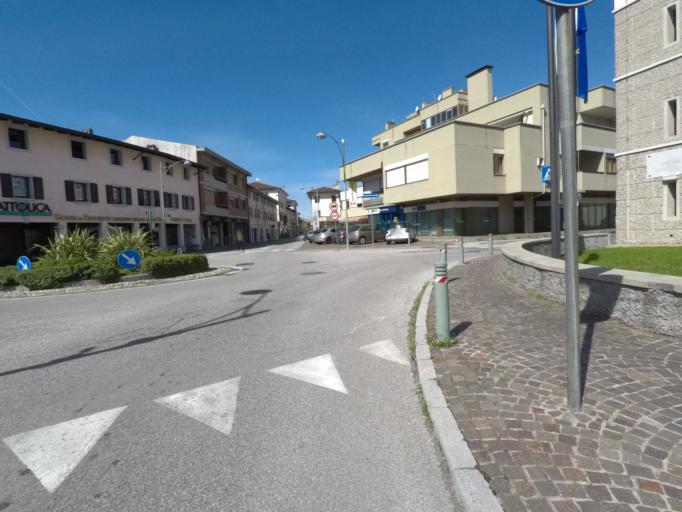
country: IT
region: Friuli Venezia Giulia
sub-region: Provincia di Udine
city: Codroipo
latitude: 45.9605
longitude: 12.9830
